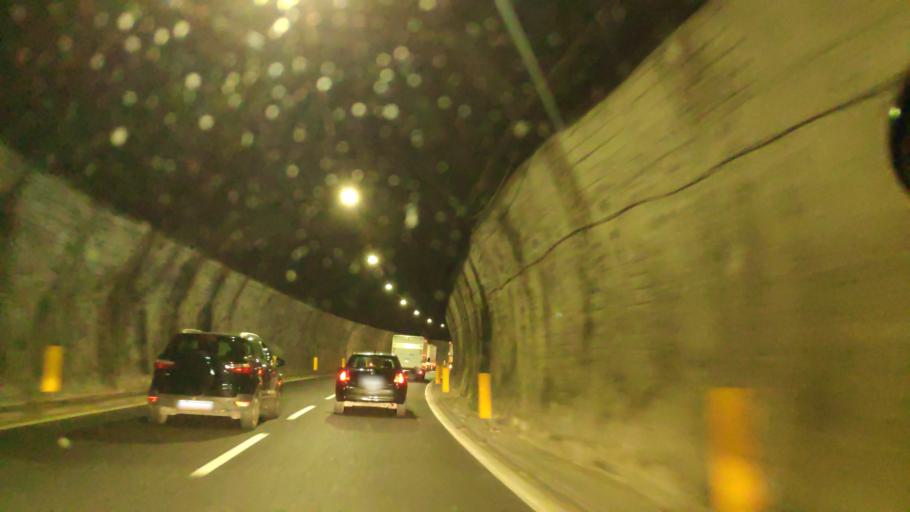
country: IT
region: Campania
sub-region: Provincia di Salerno
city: Capezzano Inferiore
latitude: 40.6867
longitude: 14.7645
